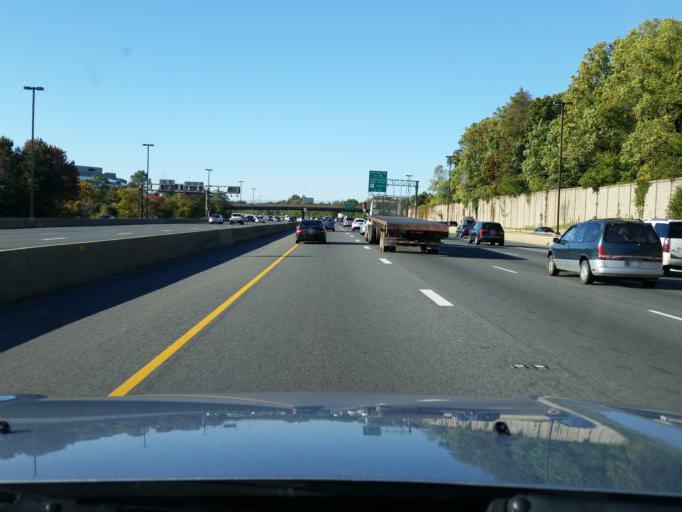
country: US
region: Maryland
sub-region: Montgomery County
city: Derwood
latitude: 39.0981
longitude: -77.1779
